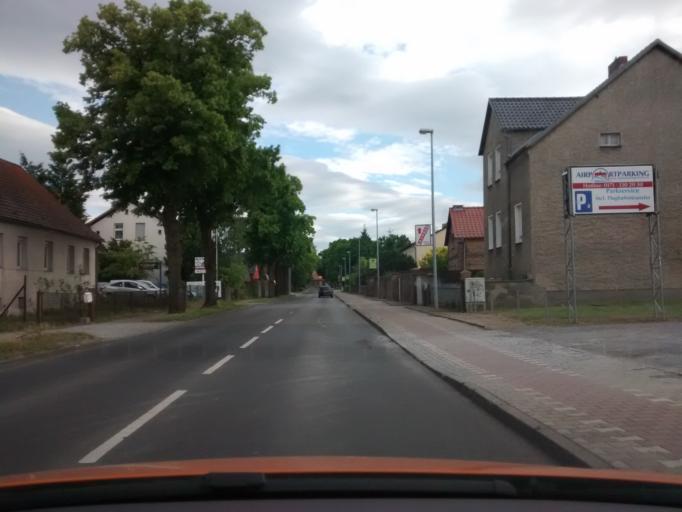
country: DE
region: Brandenburg
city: Schulzendorf
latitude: 52.3644
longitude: 13.5558
